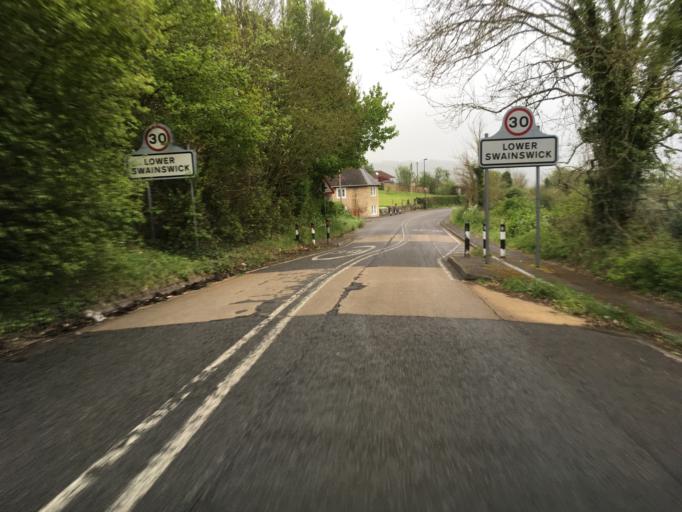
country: GB
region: England
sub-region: Bath and North East Somerset
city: Bath
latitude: 51.4049
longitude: -2.3425
